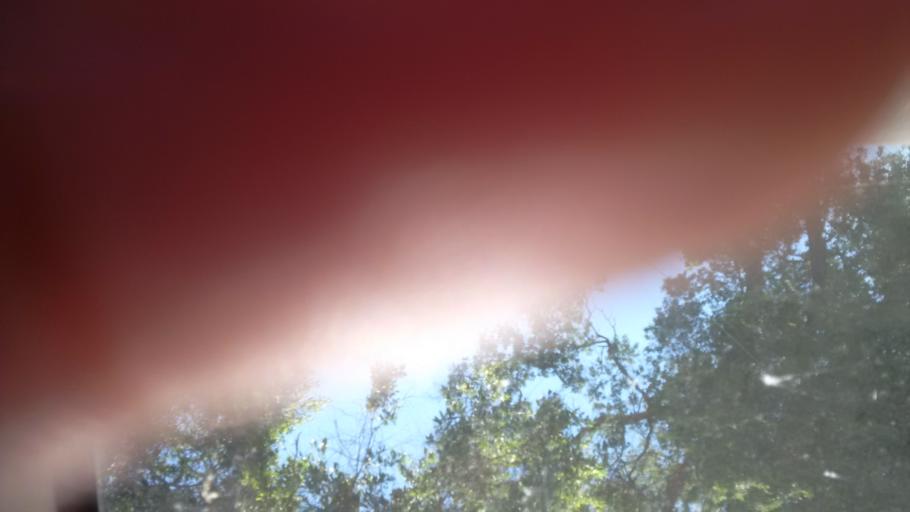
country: HT
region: Ouest
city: Thomazeau
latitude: 18.6582
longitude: -72.1481
